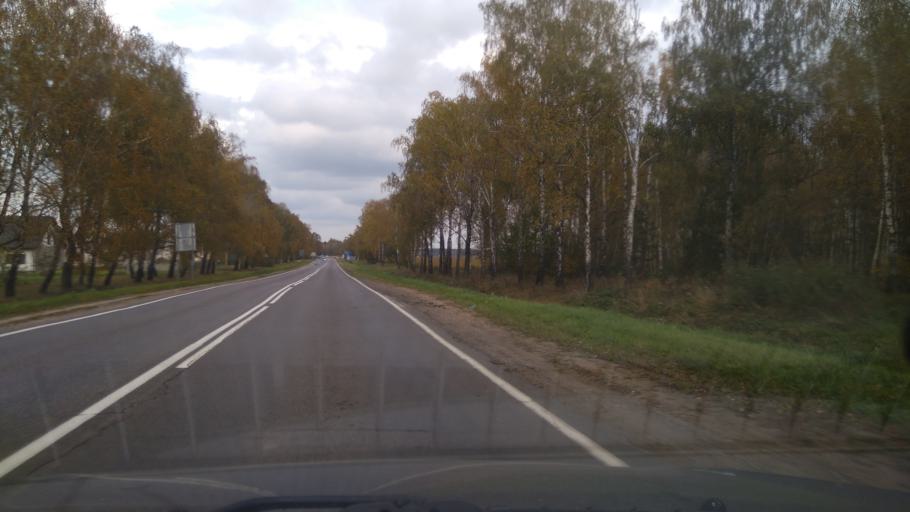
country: BY
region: Minsk
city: Svislach
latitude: 53.6538
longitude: 27.9337
